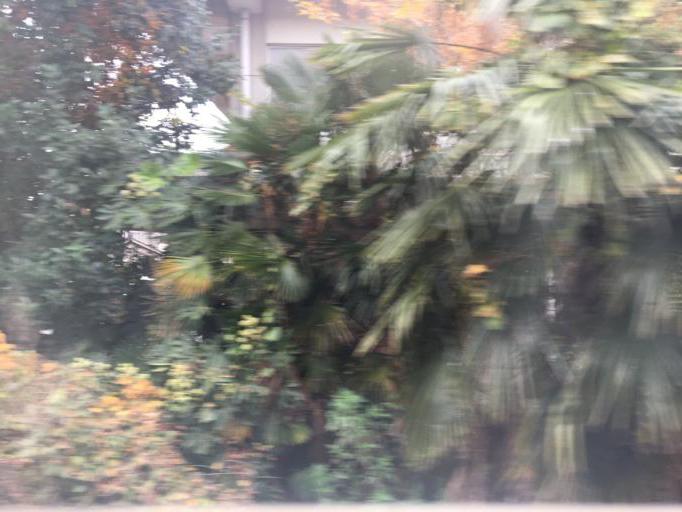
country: JP
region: Tochigi
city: Oyama
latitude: 36.3509
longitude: 139.7812
